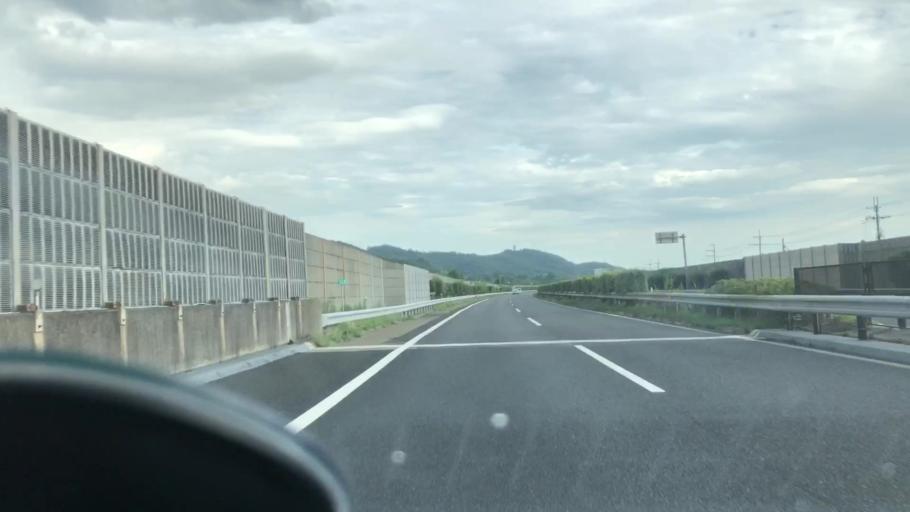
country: JP
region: Hyogo
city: Ono
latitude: 34.9387
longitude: 134.8294
